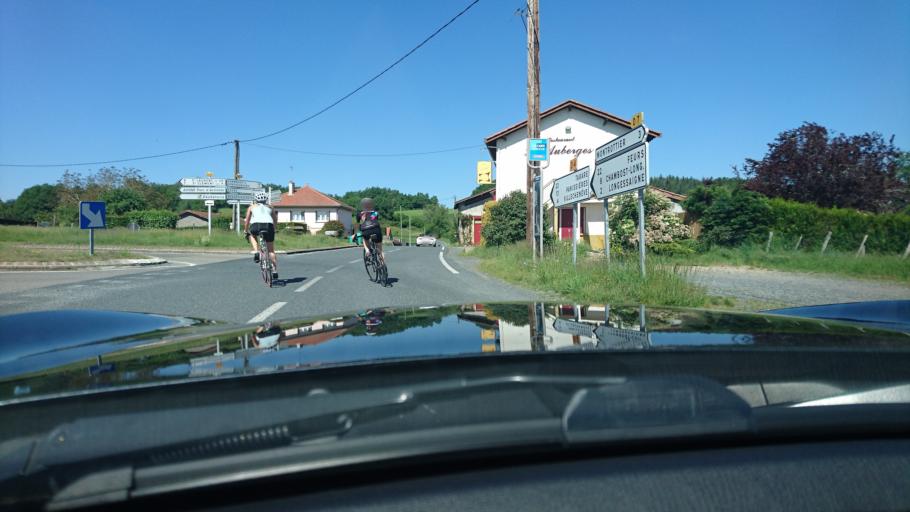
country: FR
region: Rhone-Alpes
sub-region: Departement du Rhone
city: Montrottier
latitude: 45.7933
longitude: 4.4430
